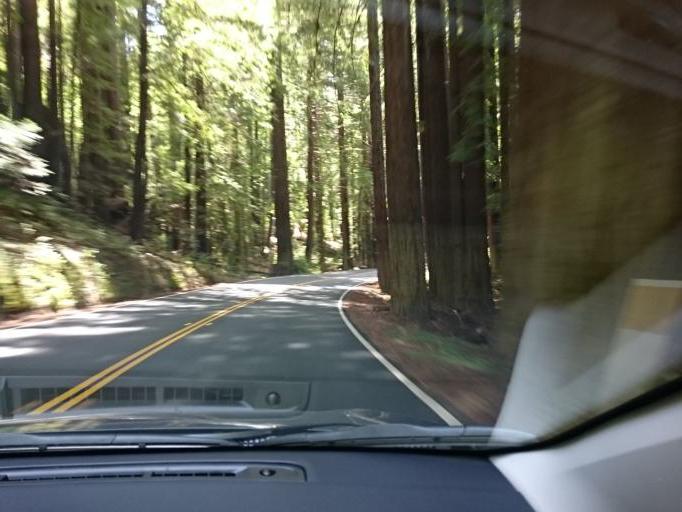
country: US
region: California
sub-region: Mendocino County
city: Boonville
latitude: 39.1593
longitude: -123.6375
